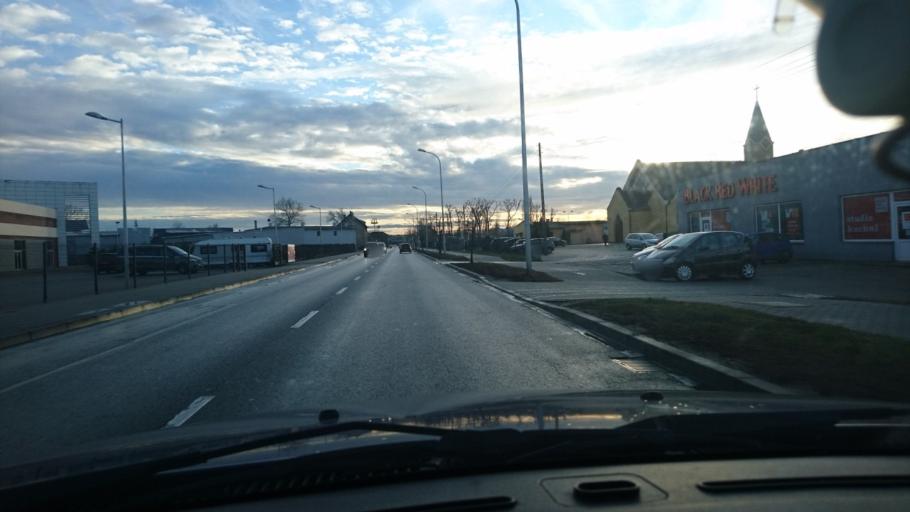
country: PL
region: Greater Poland Voivodeship
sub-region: Powiat kepinski
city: Kepno
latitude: 51.2928
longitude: 17.9953
